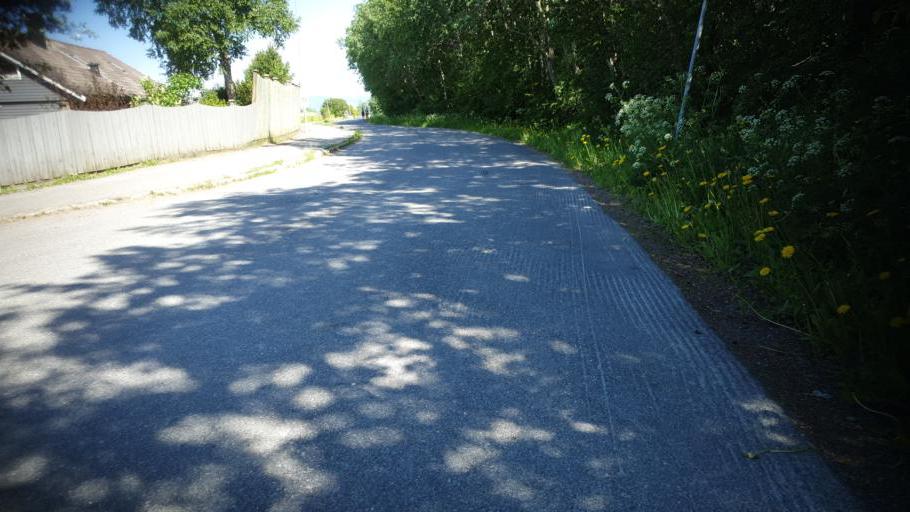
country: NO
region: Sor-Trondelag
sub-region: Malvik
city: Malvik
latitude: 63.4319
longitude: 10.6137
